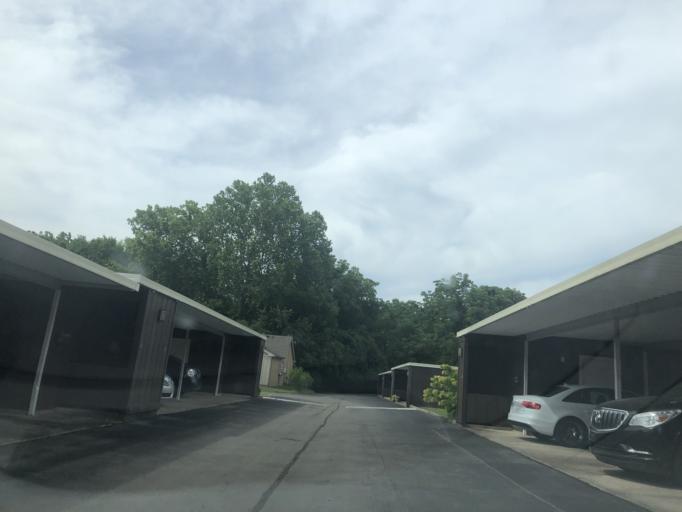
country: US
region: Tennessee
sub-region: Davidson County
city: Belle Meade
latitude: 36.0747
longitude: -86.9488
